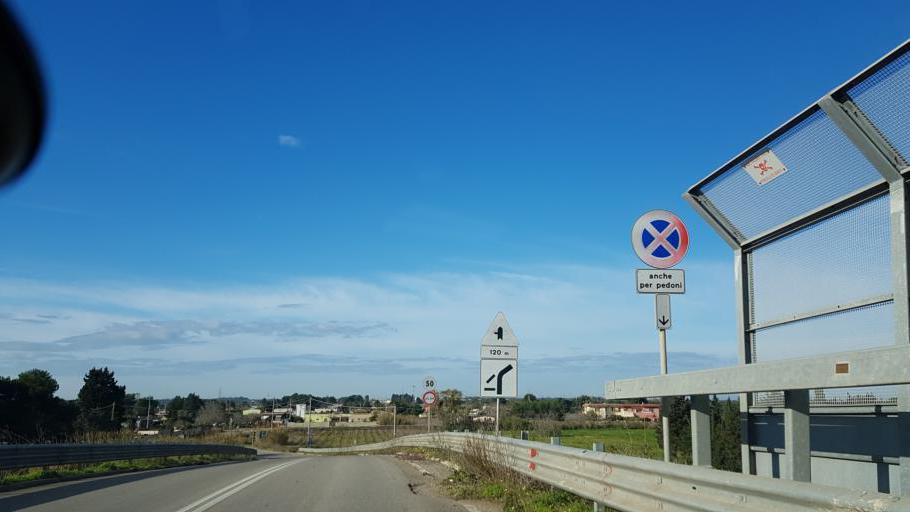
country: IT
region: Apulia
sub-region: Provincia di Brindisi
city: Tuturano
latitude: 40.5495
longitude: 17.9793
